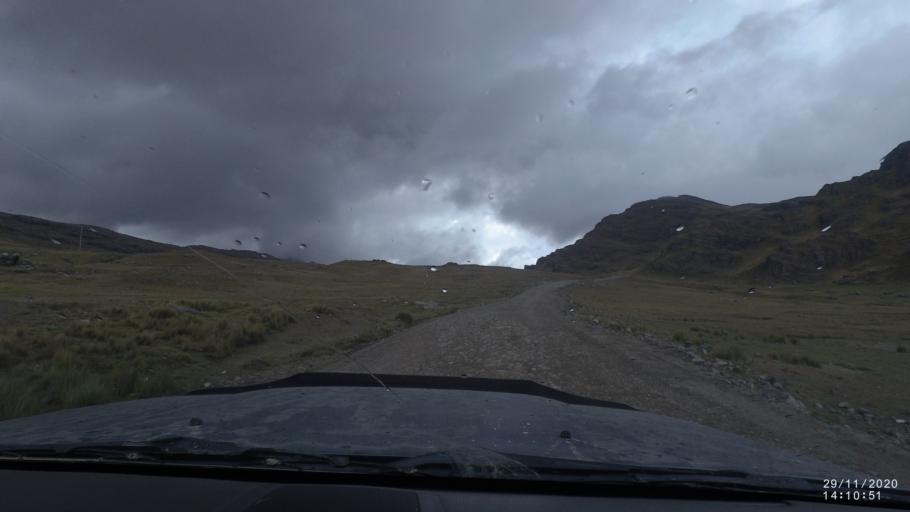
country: BO
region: Cochabamba
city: Sipe Sipe
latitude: -17.2317
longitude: -66.3903
